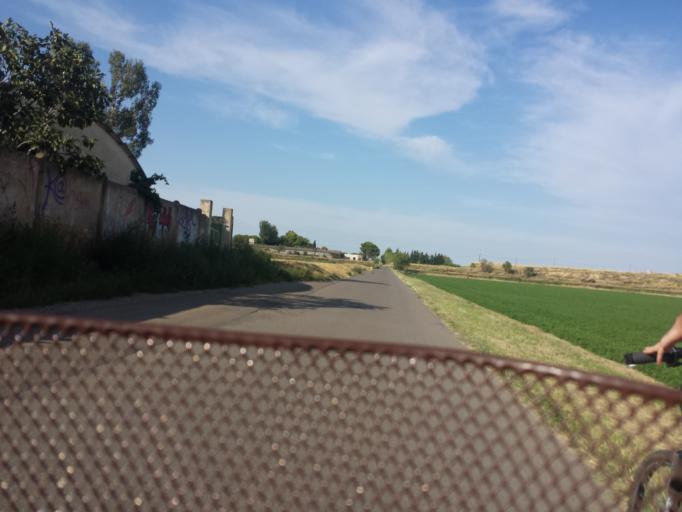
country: ES
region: Aragon
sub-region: Provincia de Zaragoza
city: Zaragoza
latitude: 41.6963
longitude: -0.8602
